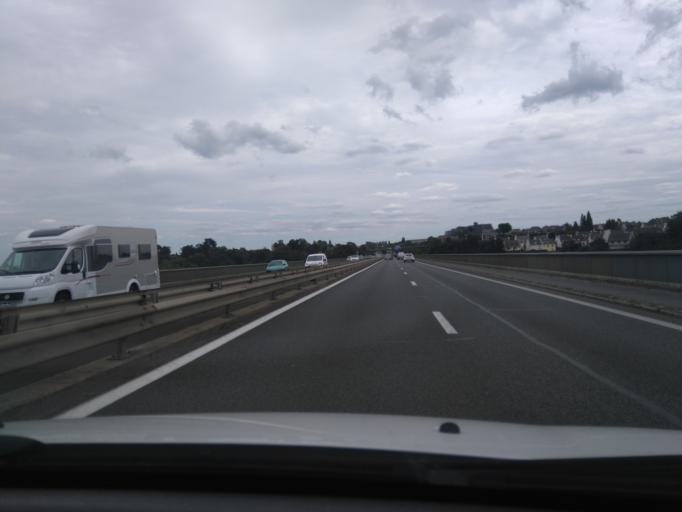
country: FR
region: Brittany
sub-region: Departement des Cotes-d'Armor
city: Saint-Brieuc
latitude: 48.5256
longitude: -2.7518
